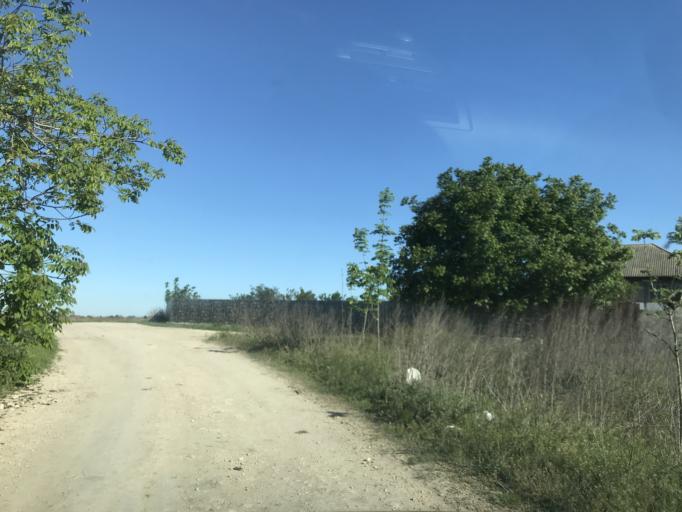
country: MD
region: Chisinau
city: Cricova
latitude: 47.2344
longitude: 28.8164
